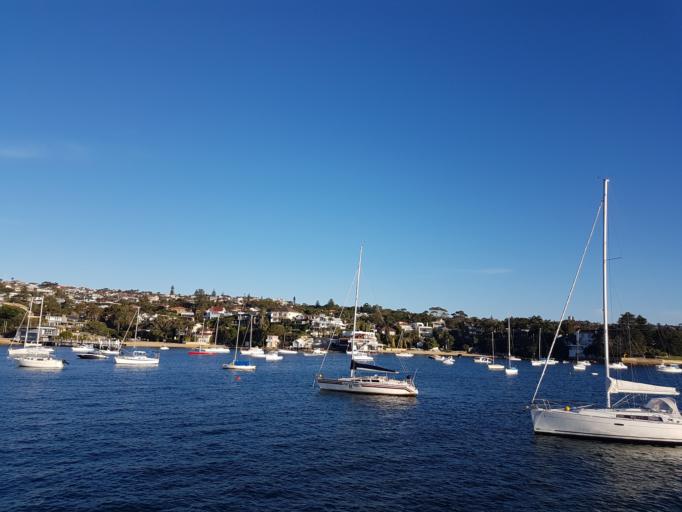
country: AU
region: New South Wales
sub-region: Waverley
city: Dover Heights
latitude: -33.8441
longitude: 151.2790
